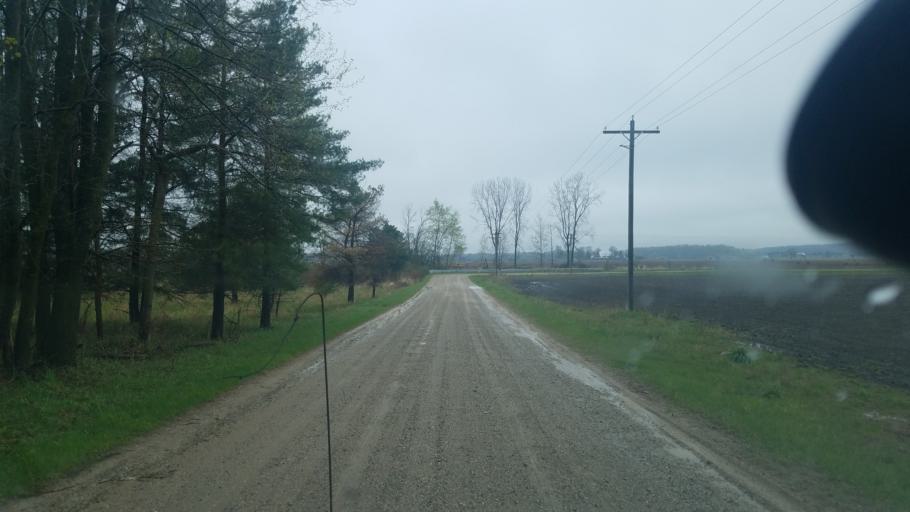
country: US
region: Michigan
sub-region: Montcalm County
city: Lakeview
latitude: 43.4807
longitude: -85.2937
